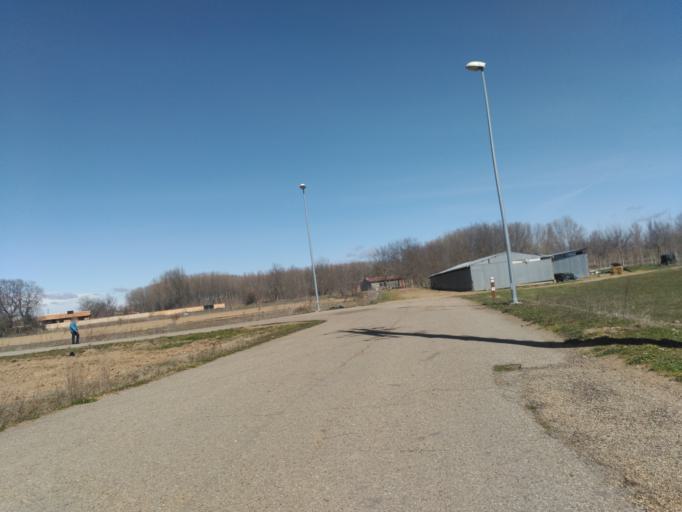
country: ES
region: Castille and Leon
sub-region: Provincia de Leon
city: Hospital de Orbigo
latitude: 42.4403
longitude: -5.8792
